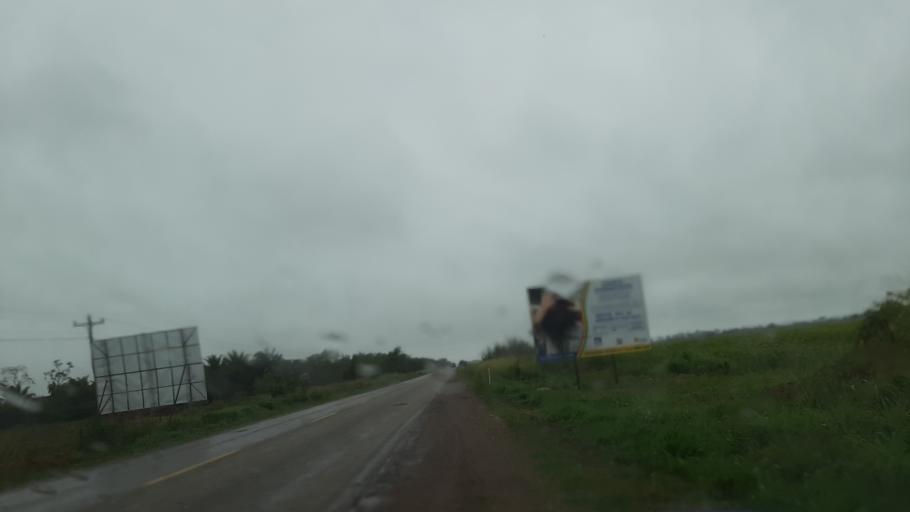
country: BO
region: Santa Cruz
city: Okinawa Numero Uno
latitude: -16.8025
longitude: -62.5978
